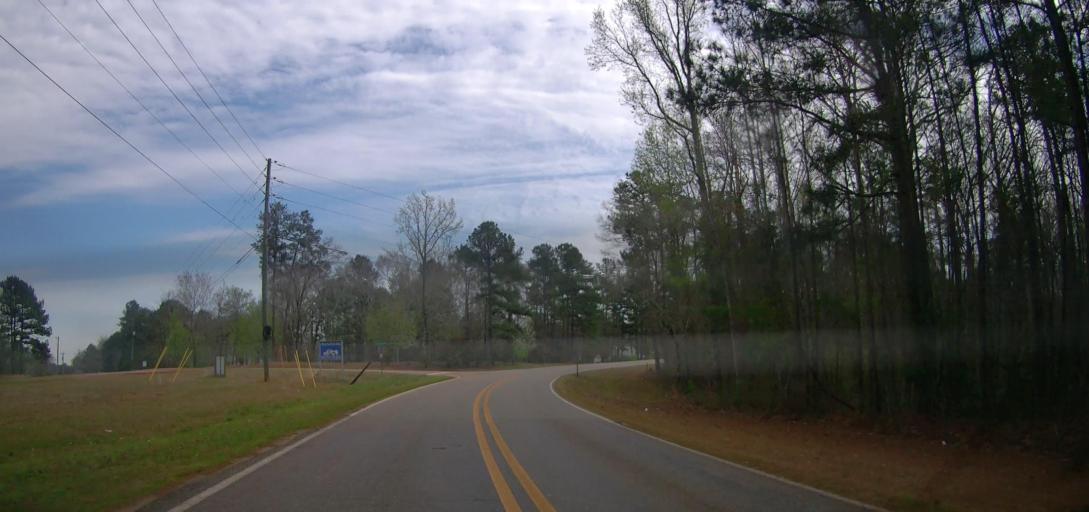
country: US
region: Georgia
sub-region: Bibb County
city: Macon
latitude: 32.9634
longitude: -83.6601
